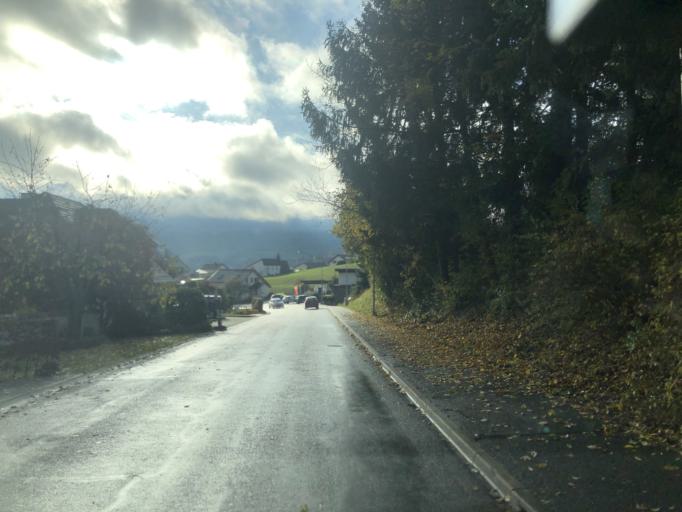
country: CH
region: Aargau
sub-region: Bezirk Baden
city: Unterehrendingen
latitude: 47.5180
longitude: 8.3649
